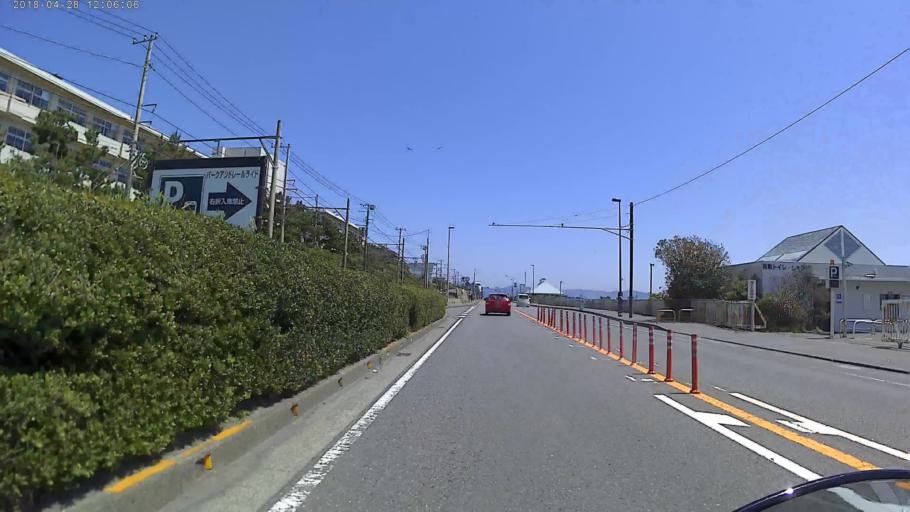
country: JP
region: Kanagawa
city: Kamakura
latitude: 35.3052
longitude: 139.5116
